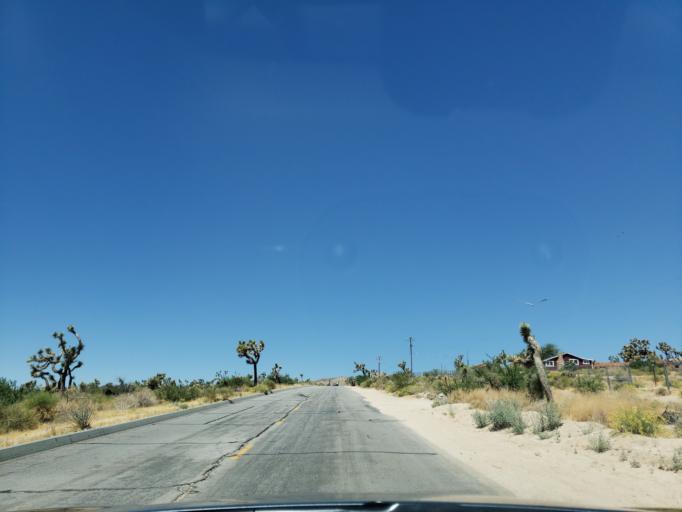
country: US
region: California
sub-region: San Bernardino County
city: Yucca Valley
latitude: 34.1351
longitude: -116.4000
